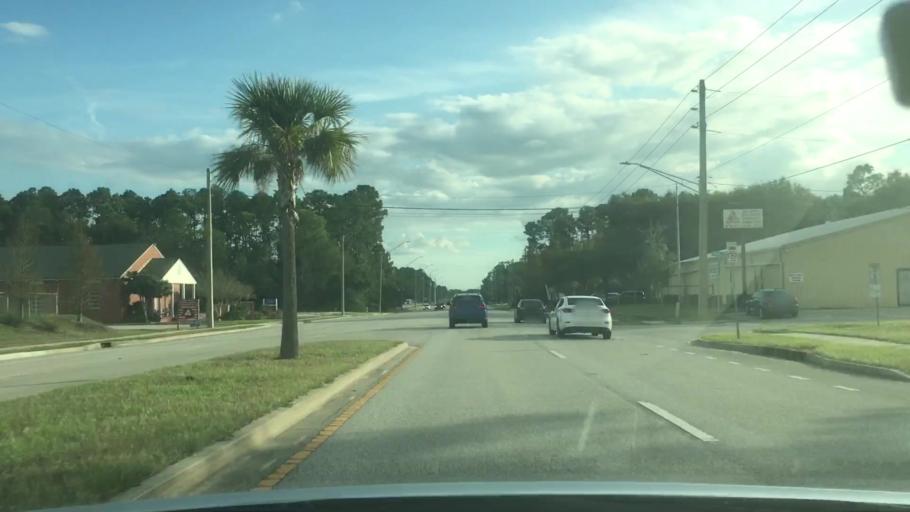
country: US
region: Florida
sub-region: Duval County
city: Atlantic Beach
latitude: 30.3349
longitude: -81.5234
